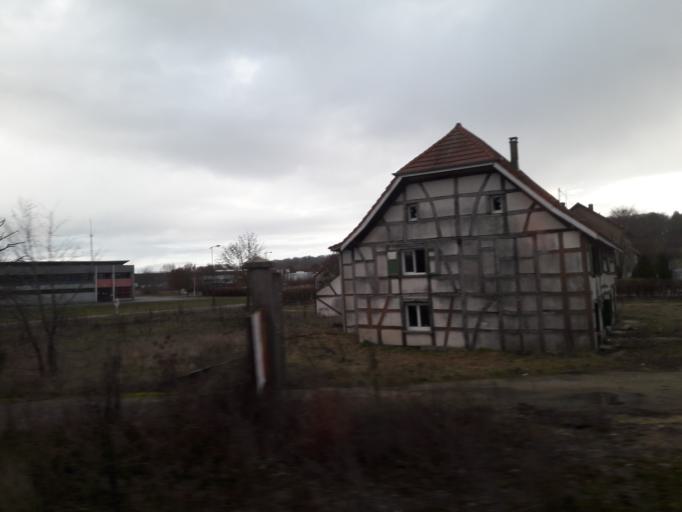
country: FR
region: Franche-Comte
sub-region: Territoire de Belfort
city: Morvillars
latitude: 47.5560
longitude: 6.9277
